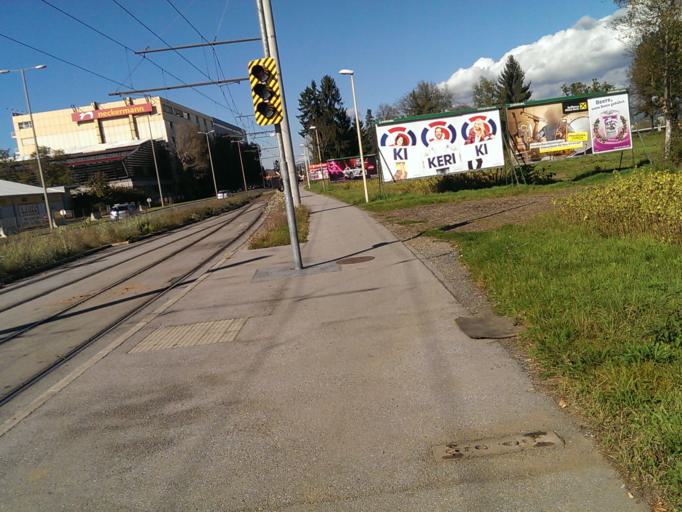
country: AT
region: Styria
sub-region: Politischer Bezirk Graz-Umgebung
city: Feldkirchen bei Graz
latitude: 47.0331
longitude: 15.4316
